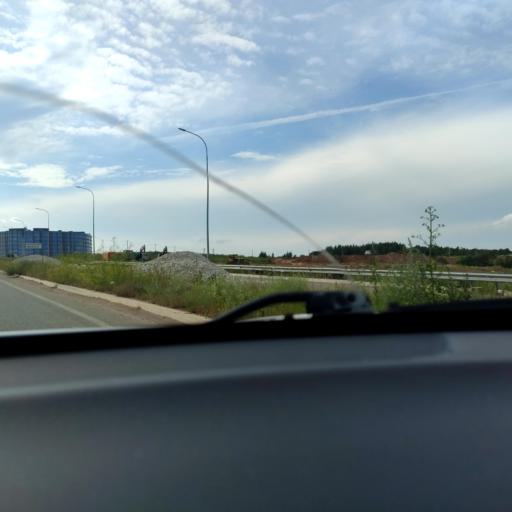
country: RU
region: Tatarstan
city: Sviyazhsk
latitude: 55.7484
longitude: 48.7604
